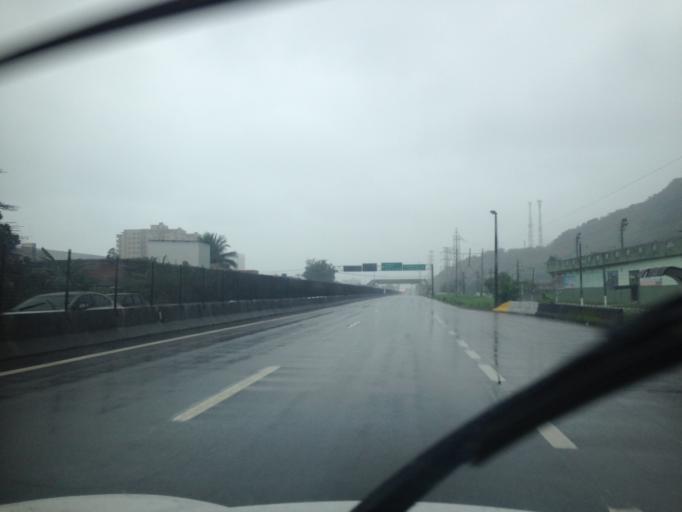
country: BR
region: Sao Paulo
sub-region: Mongagua
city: Mongagua
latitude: -24.0952
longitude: -46.6263
